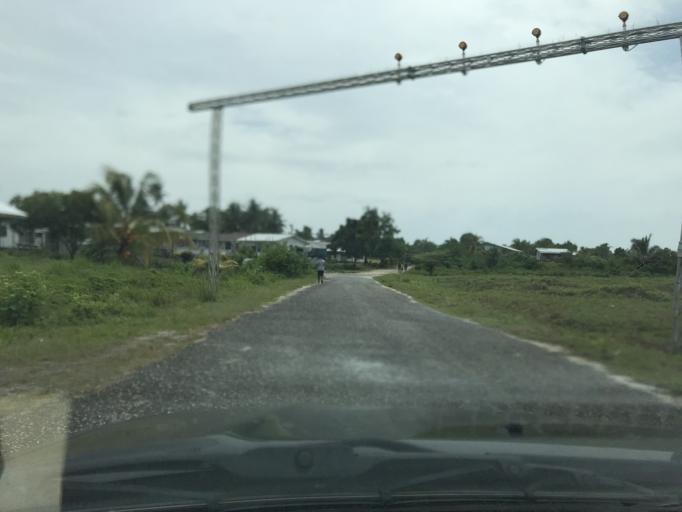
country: SB
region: Western Province
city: Gizo
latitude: -8.3292
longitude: 157.2512
